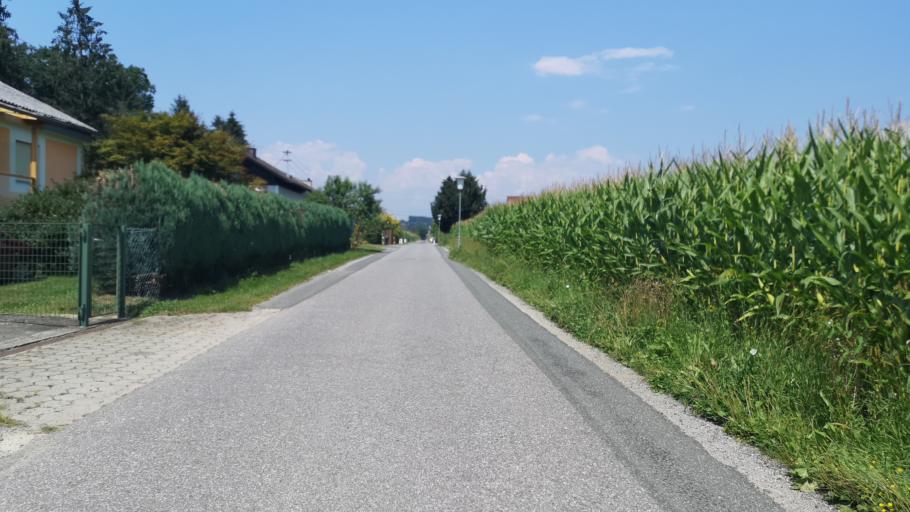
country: AT
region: Styria
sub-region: Politischer Bezirk Deutschlandsberg
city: Rassach
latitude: 46.8139
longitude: 15.2708
